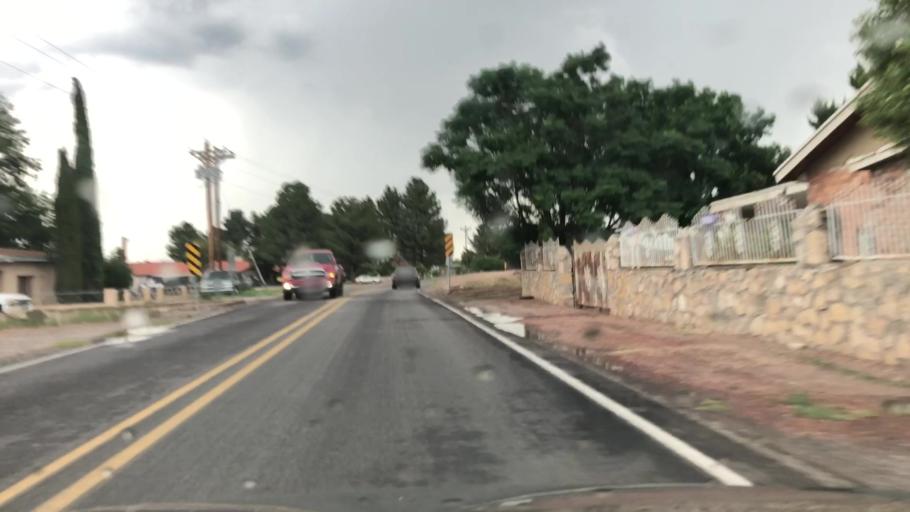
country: US
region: New Mexico
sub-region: Dona Ana County
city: Berino
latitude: 32.0507
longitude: -106.6755
